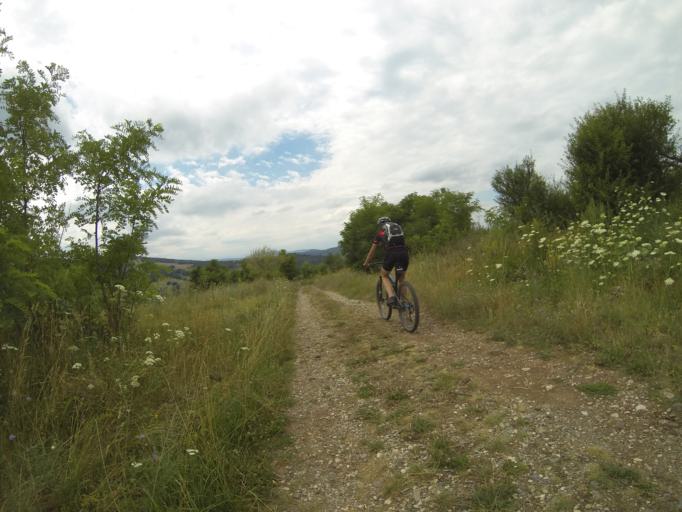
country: RO
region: Covasna
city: Racosu de Sus
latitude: 46.0304
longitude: 25.4203
